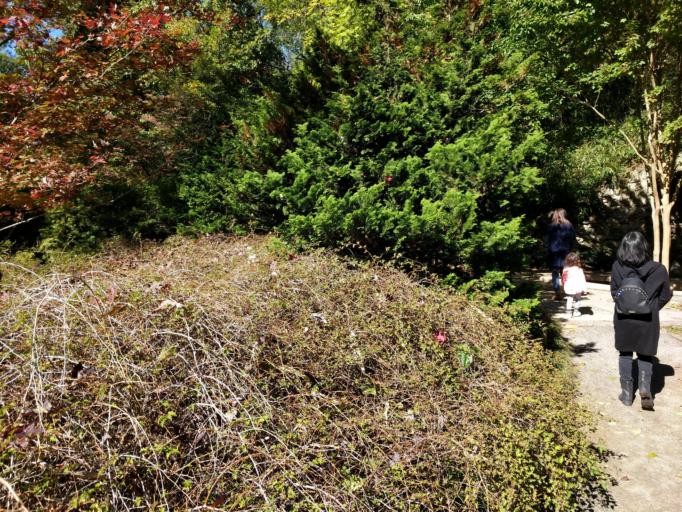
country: US
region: Virginia
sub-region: City of Richmond
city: Richmond
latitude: 37.5329
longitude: -77.4761
